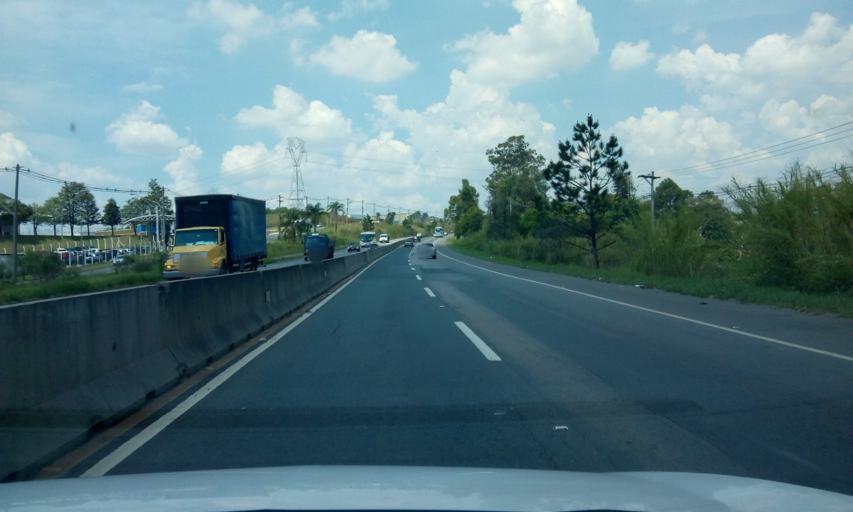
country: BR
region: Sao Paulo
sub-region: Itupeva
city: Itupeva
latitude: -23.1628
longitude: -47.0172
